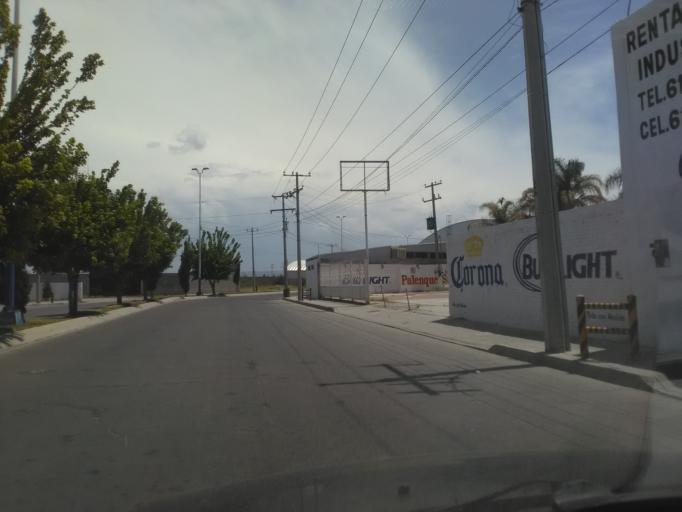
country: MX
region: Durango
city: Victoria de Durango
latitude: 24.0280
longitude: -104.6143
